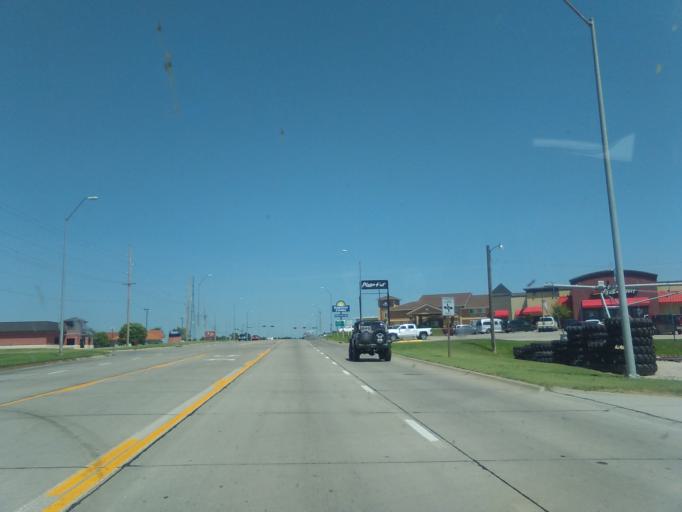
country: US
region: Nebraska
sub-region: Red Willow County
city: McCook
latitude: 40.2048
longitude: -100.6464
